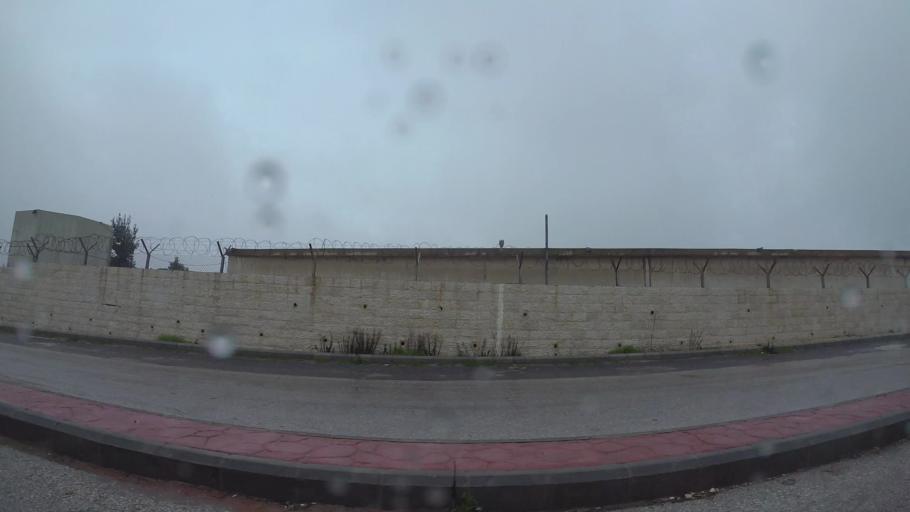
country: JO
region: Amman
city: Al Jubayhah
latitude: 32.0028
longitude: 35.8224
